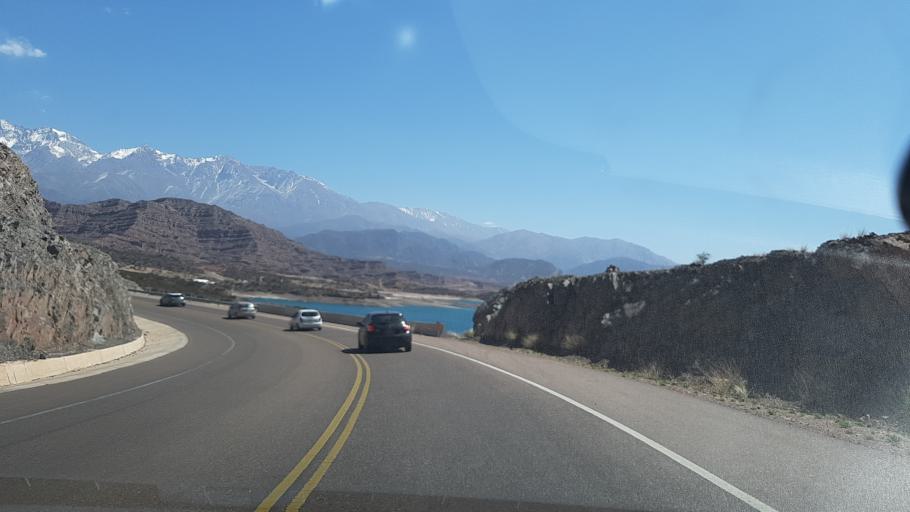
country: AR
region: Mendoza
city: Lujan de Cuyo
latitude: -32.9919
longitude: -69.1541
